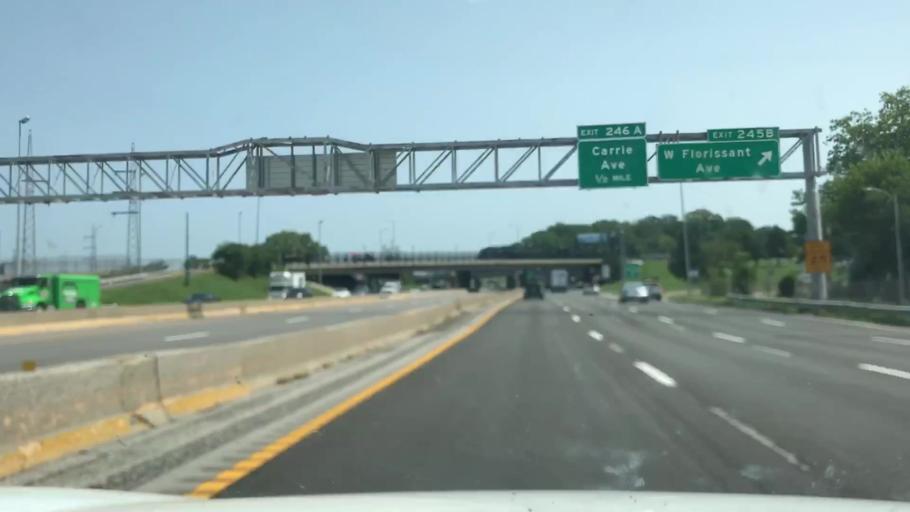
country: US
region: Missouri
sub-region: Saint Louis County
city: Pine Lawn
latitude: 38.6829
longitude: -90.2304
